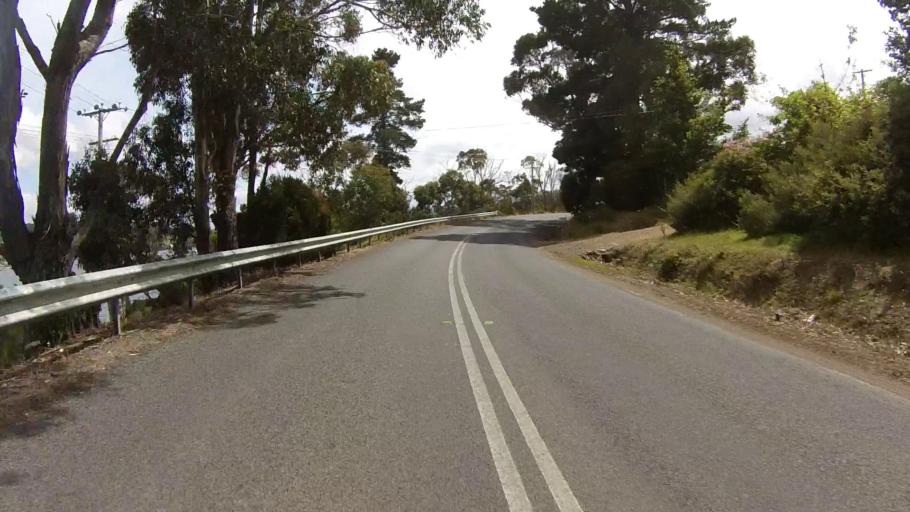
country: AU
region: Tasmania
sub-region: Huon Valley
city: Cygnet
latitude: -43.1806
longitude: 147.0928
